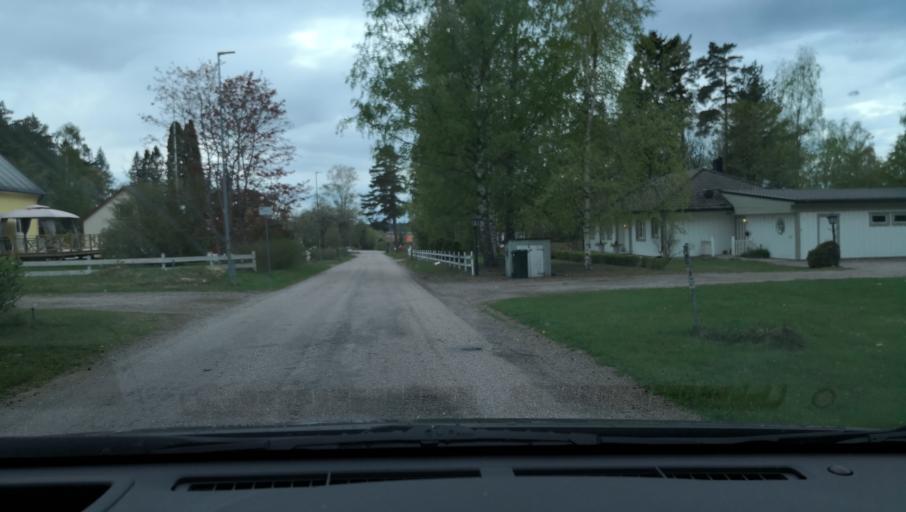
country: SE
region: Dalarna
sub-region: Avesta Kommun
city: Avesta
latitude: 60.0254
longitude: 16.3304
